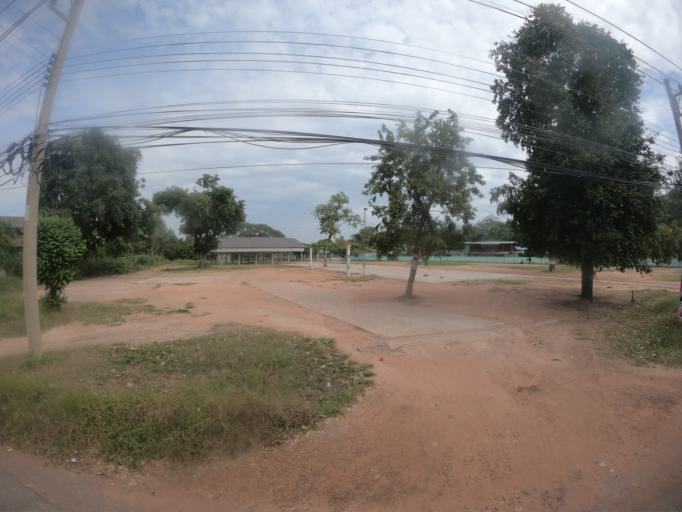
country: TH
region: Maha Sarakham
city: Chiang Yuen
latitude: 16.3456
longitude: 103.1237
